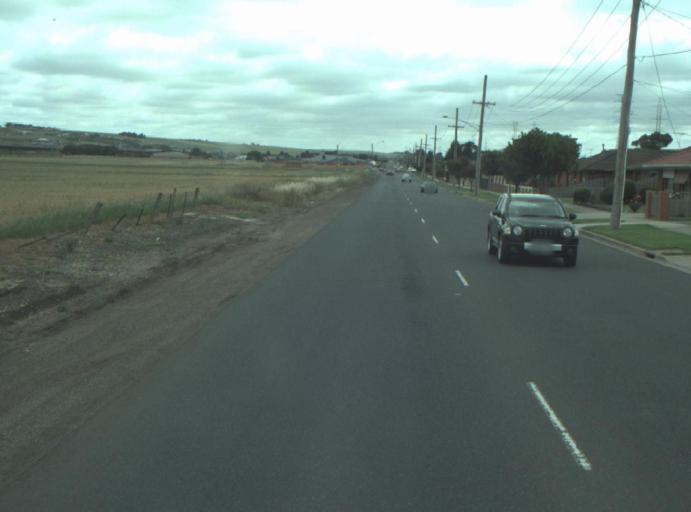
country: AU
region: Victoria
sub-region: Greater Geelong
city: Bell Post Hill
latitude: -38.0791
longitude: 144.3377
